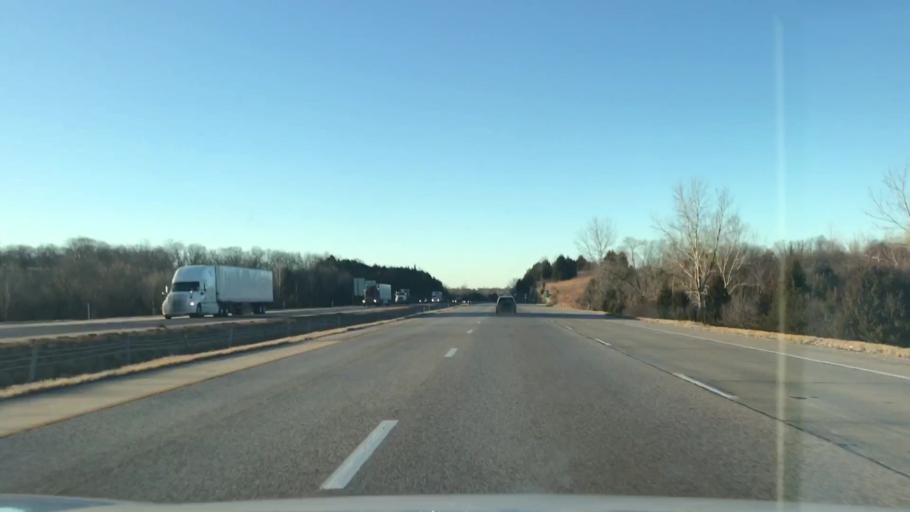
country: US
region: Missouri
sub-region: Franklin County
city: Villa Ridge
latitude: 38.4717
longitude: -90.8529
